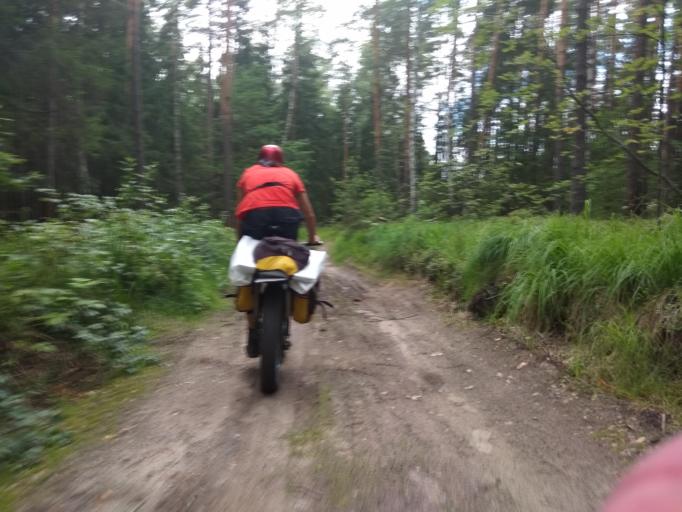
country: RU
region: Moskovskaya
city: Misheronskiy
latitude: 55.6376
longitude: 39.7218
